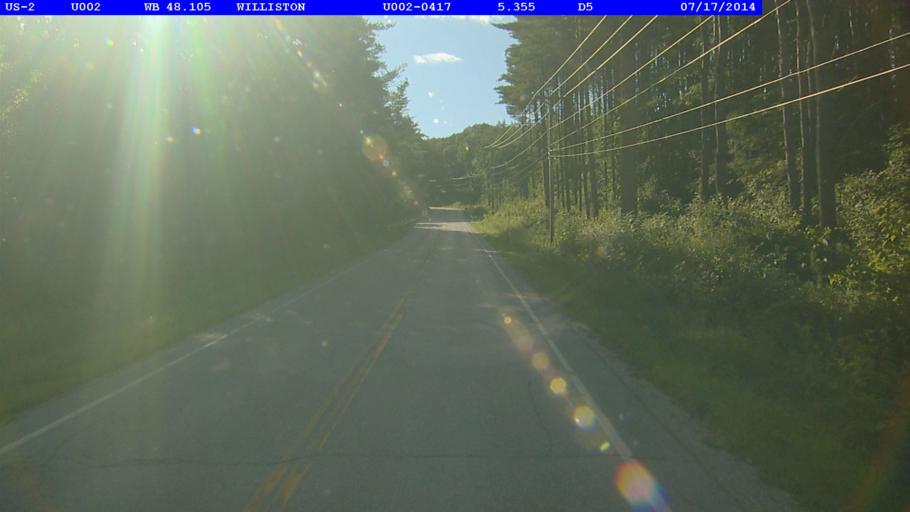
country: US
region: Vermont
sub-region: Chittenden County
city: Williston
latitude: 44.4340
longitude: -73.0370
